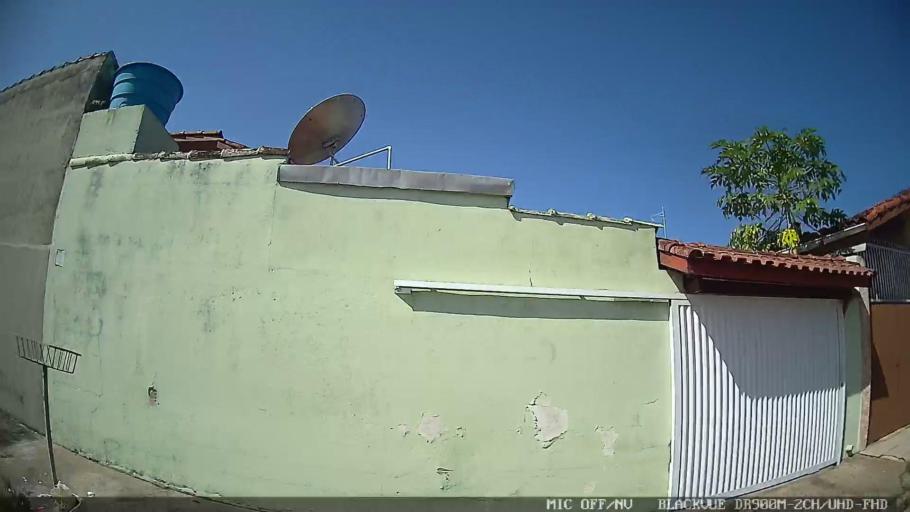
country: BR
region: Sao Paulo
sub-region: Peruibe
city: Peruibe
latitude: -24.3129
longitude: -46.9950
